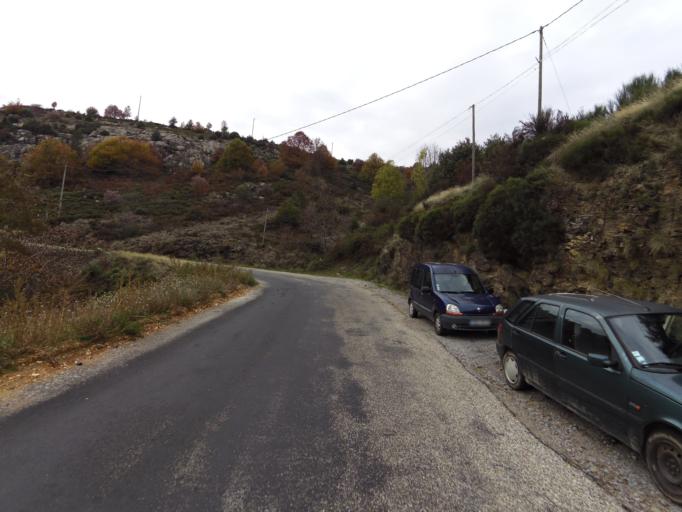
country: FR
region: Rhone-Alpes
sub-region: Departement de l'Ardeche
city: Les Vans
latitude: 44.5096
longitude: 4.0525
